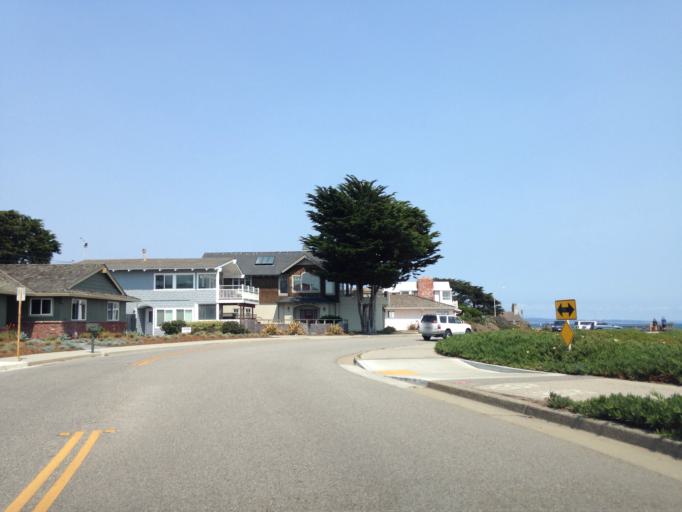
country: US
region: California
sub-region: Santa Cruz County
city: Santa Cruz
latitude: 36.9498
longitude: -122.0519
